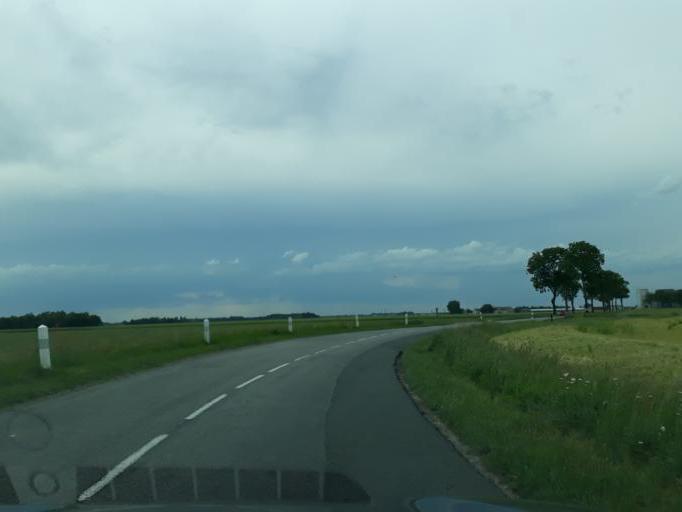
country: FR
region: Centre
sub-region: Departement du Loiret
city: Tigy
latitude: 47.8082
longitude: 2.1768
